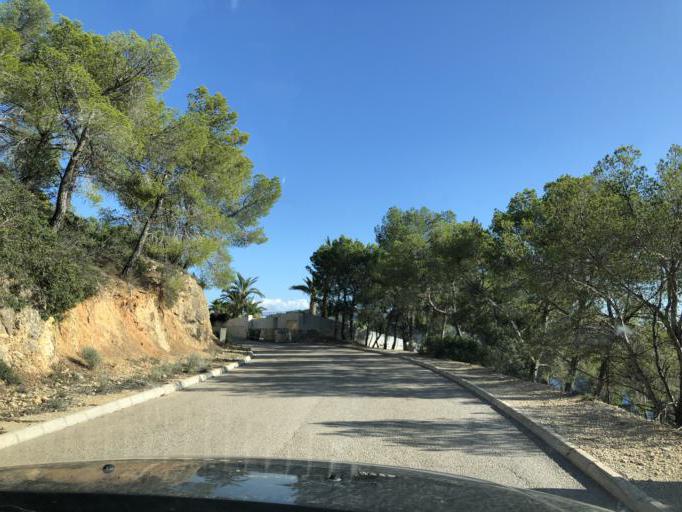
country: ES
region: Balearic Islands
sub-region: Illes Balears
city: Camp de Mar
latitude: 39.5384
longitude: 2.4068
